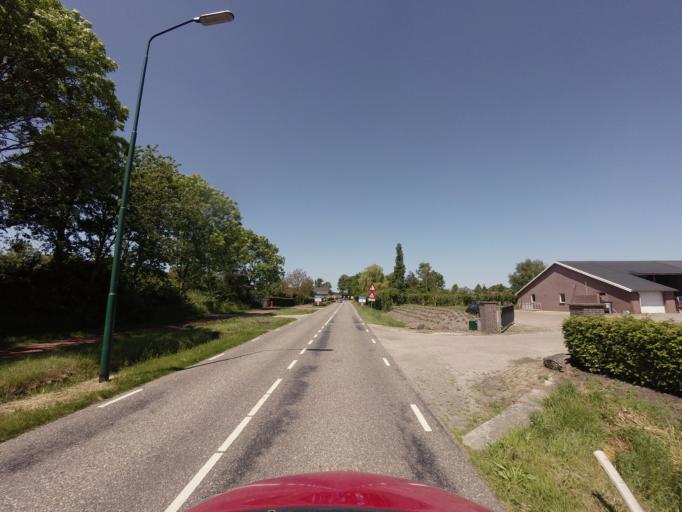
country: BE
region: Flanders
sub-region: Provincie Limburg
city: Lommel
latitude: 51.2820
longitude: 5.3148
